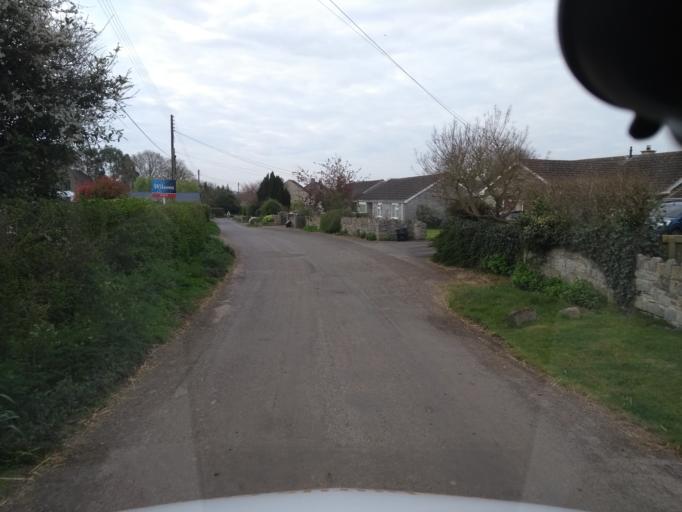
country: GB
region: England
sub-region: Somerset
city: Ilminster
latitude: 50.9805
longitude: -2.9660
